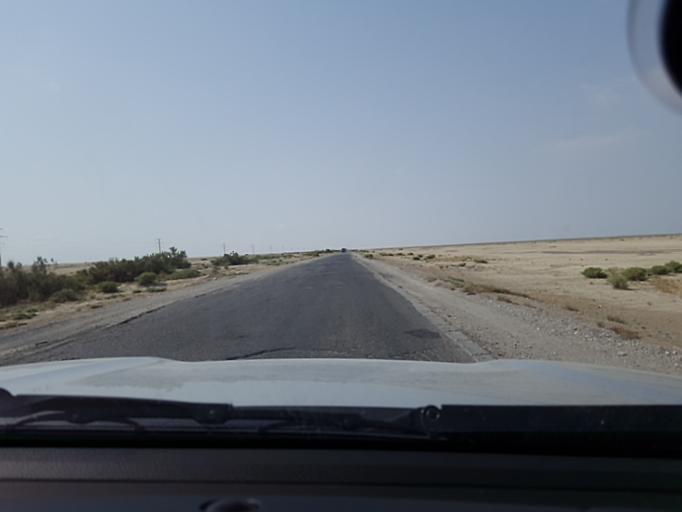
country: TM
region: Balkan
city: Gumdag
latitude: 38.9806
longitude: 54.5874
